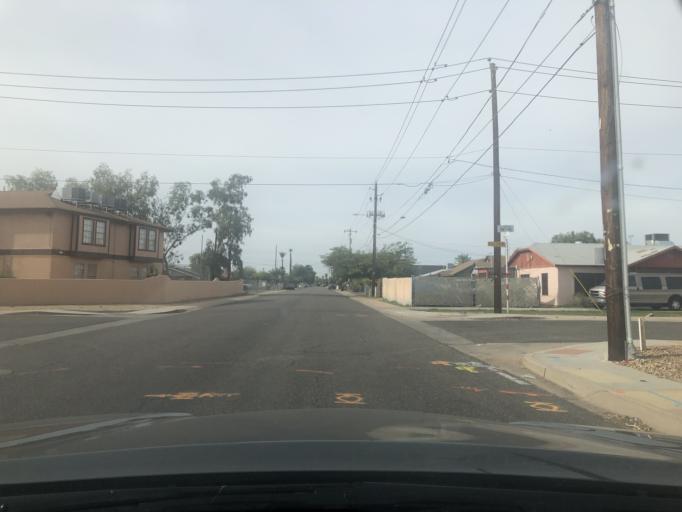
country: US
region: Arizona
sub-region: Maricopa County
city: Phoenix
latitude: 33.4604
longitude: -112.0408
